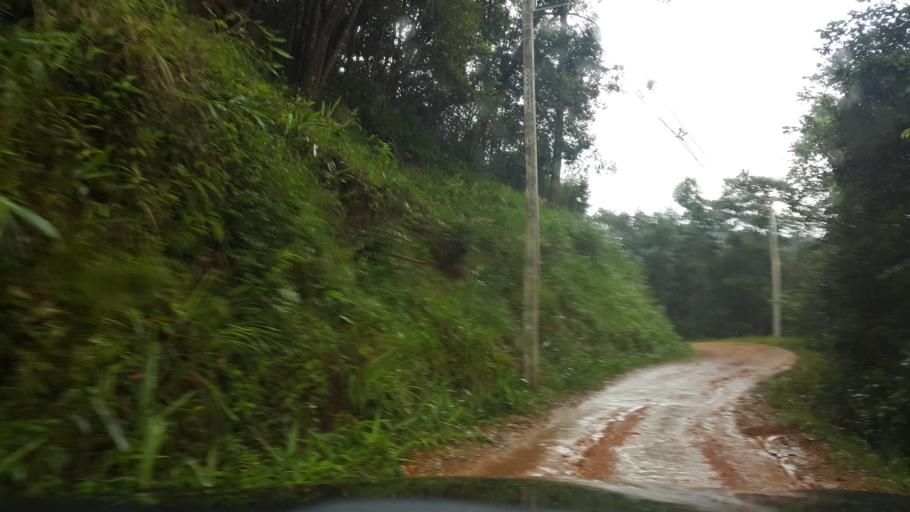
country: TH
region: Lampang
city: Wang Nuea
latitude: 19.1289
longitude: 99.3614
